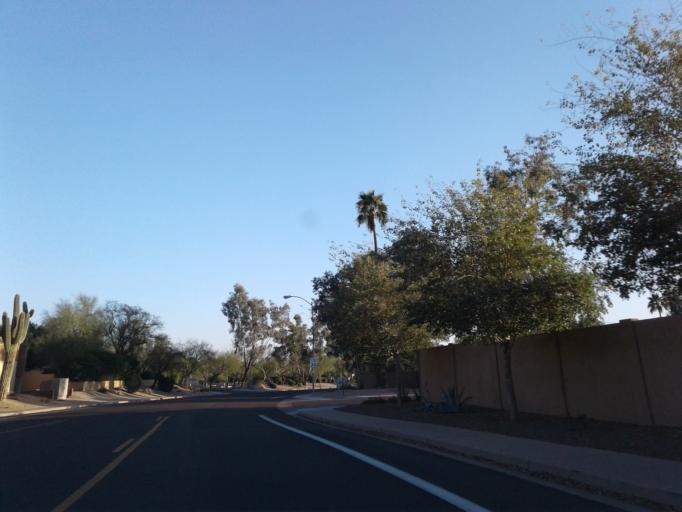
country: US
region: Arizona
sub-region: Maricopa County
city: Paradise Valley
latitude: 33.5814
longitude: -111.9178
